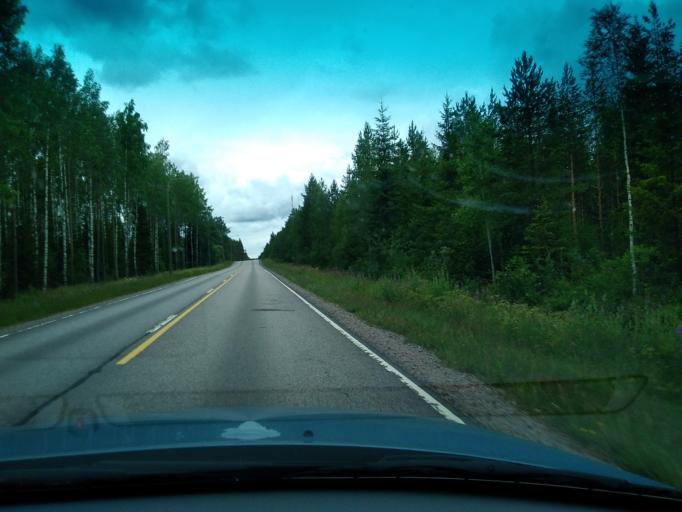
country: FI
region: Central Finland
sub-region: Saarijaervi-Viitasaari
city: Pylkoenmaeki
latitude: 62.6338
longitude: 24.8111
